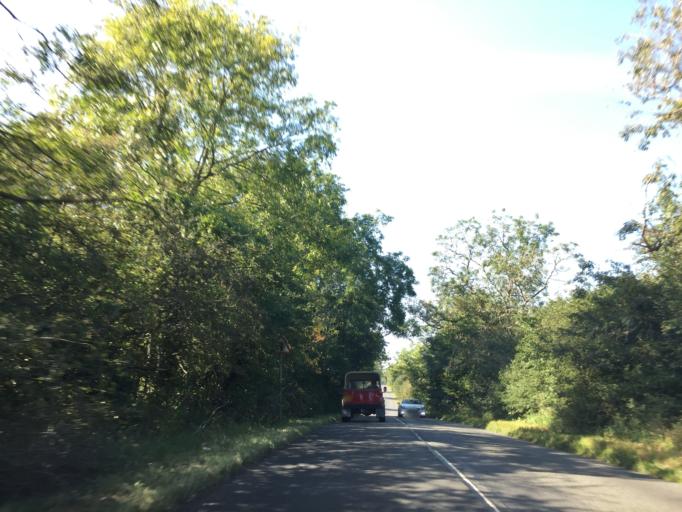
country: GB
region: England
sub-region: Leicestershire
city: Asfordby
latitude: 52.6930
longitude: -0.9813
